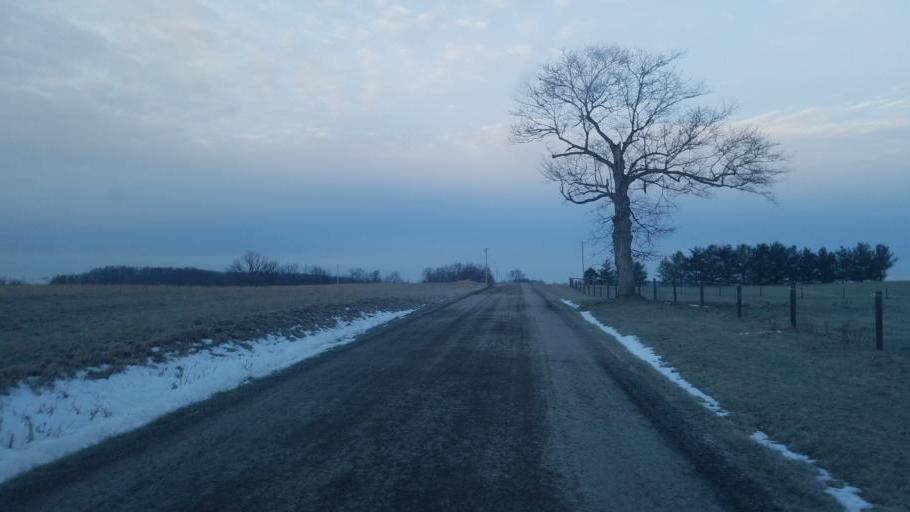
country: US
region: Ohio
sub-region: Morrow County
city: Mount Gilead
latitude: 40.4809
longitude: -82.6993
